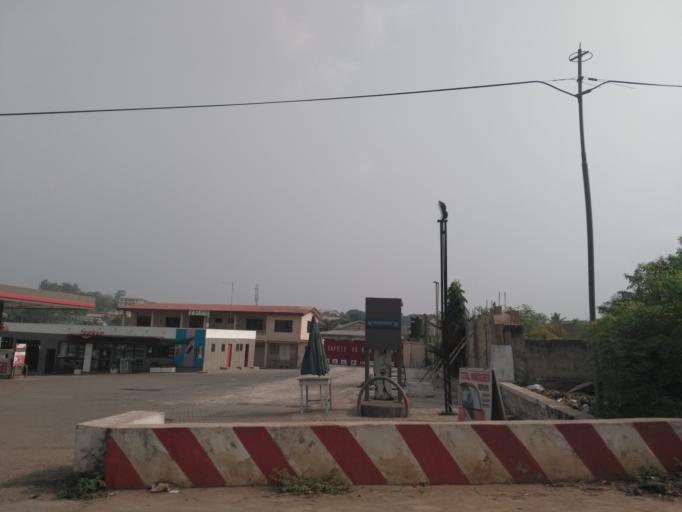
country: GH
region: Ashanti
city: Kumasi
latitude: 6.6438
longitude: -1.5720
